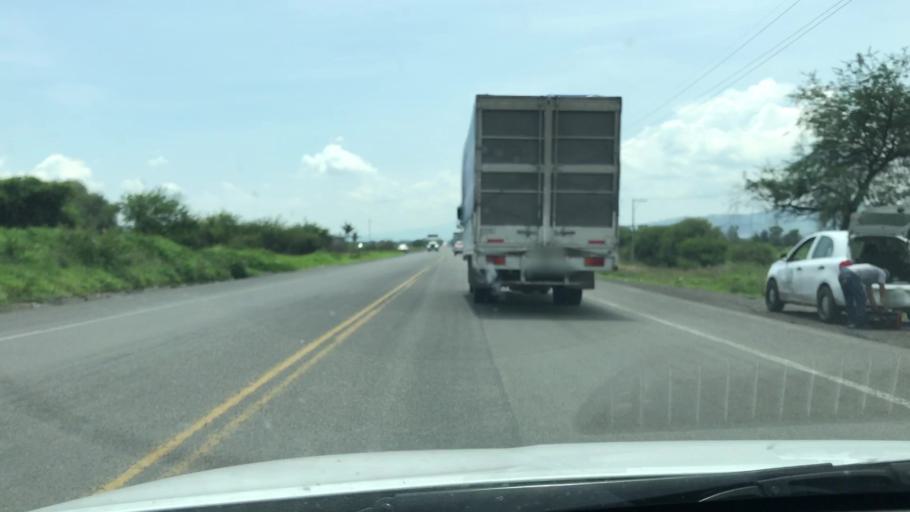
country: MX
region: Michoacan
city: Vistahermosa de Negrete
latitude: 20.2706
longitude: -102.4317
